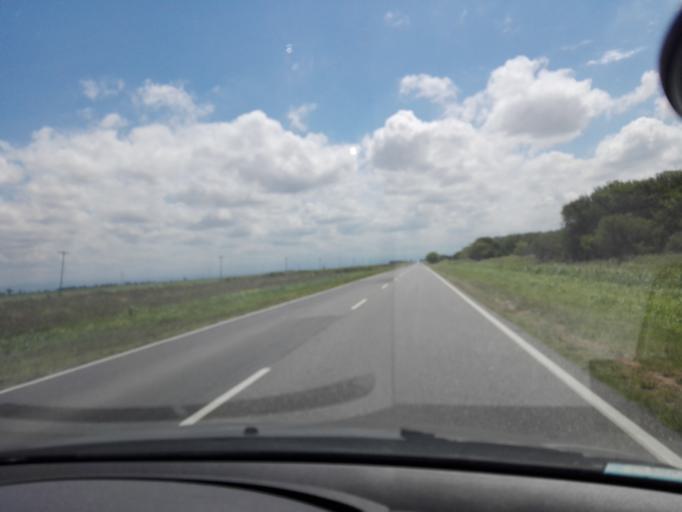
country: AR
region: Cordoba
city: Toledo
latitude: -31.6487
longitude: -64.1155
